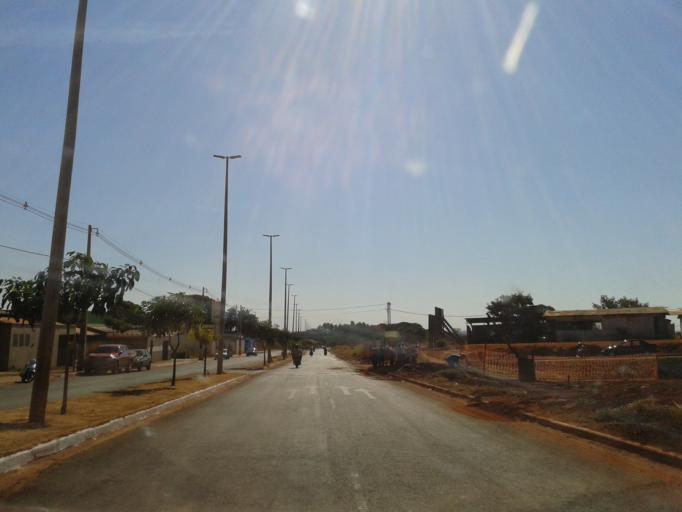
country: BR
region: Minas Gerais
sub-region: Ituiutaba
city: Ituiutaba
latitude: -18.9766
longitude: -49.4399
